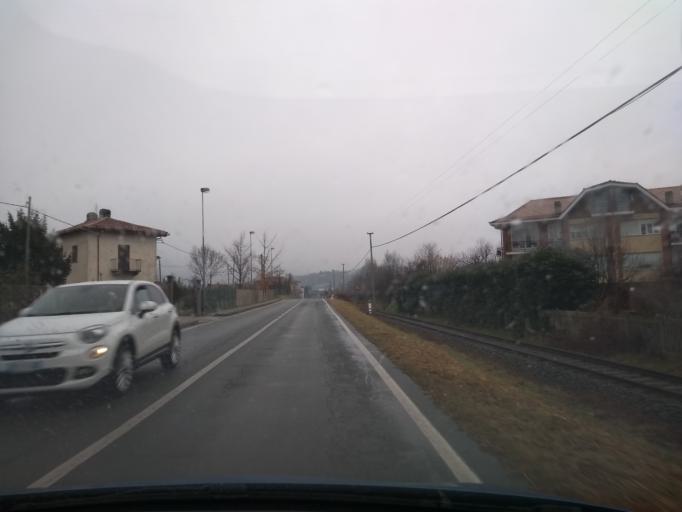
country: IT
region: Piedmont
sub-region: Provincia di Torino
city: Valperga
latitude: 45.3783
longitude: 7.6590
